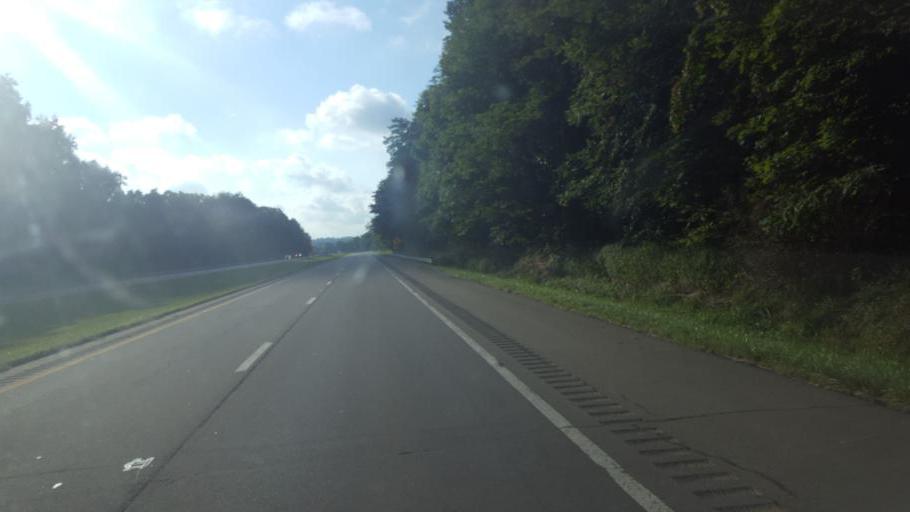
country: US
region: Ohio
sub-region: Wayne County
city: Wooster
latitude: 40.7960
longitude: -81.9989
